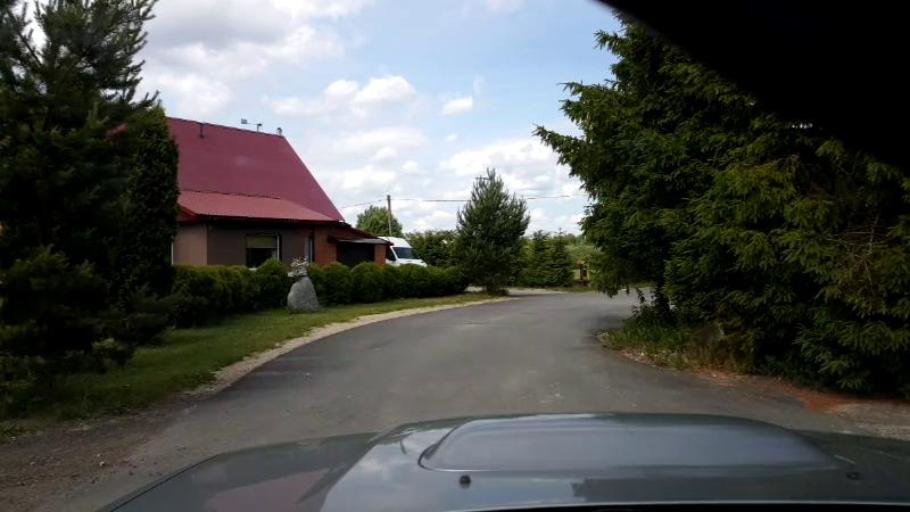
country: EE
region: Paernumaa
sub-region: Halinga vald
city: Parnu-Jaagupi
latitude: 58.5181
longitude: 24.5597
